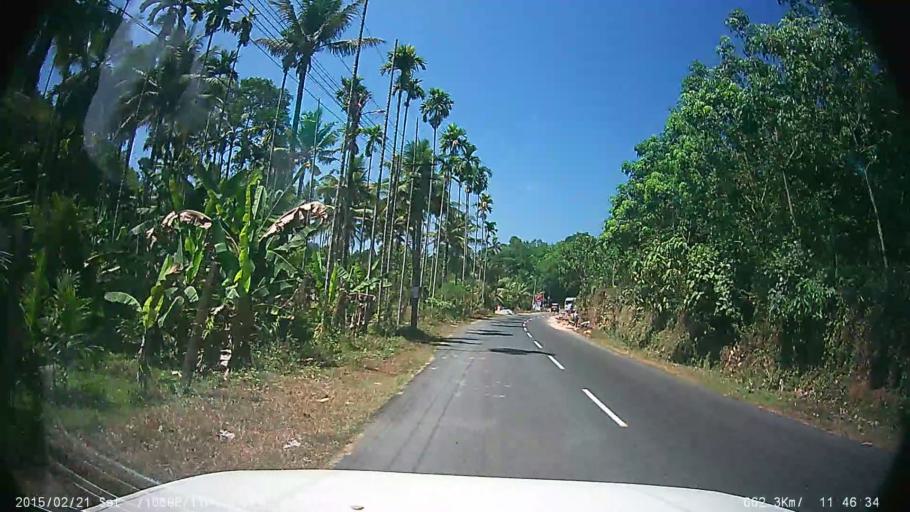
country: IN
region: Kerala
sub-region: Kottayam
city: Lalam
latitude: 9.7769
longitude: 76.7214
